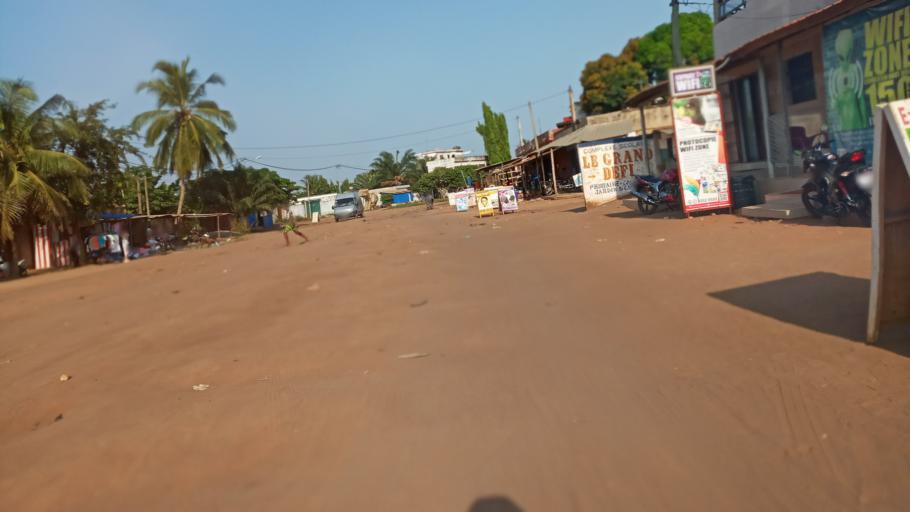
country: TG
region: Maritime
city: Lome
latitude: 6.1810
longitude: 1.1549
